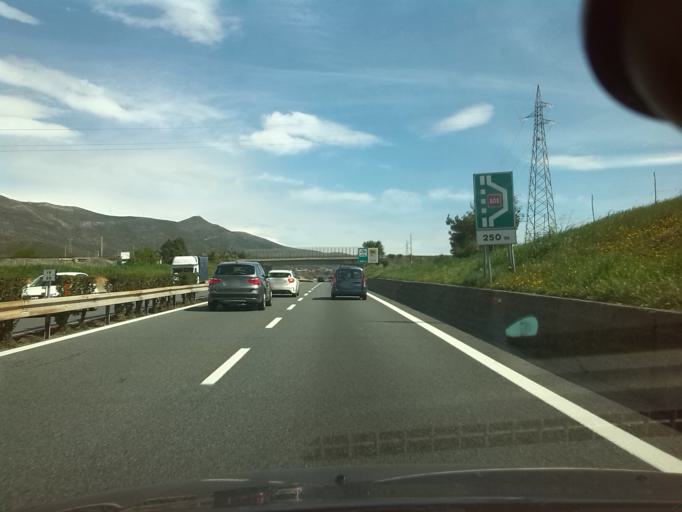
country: IT
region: Liguria
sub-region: Provincia di Savona
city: Campochiesa
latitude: 44.0698
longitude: 8.1801
